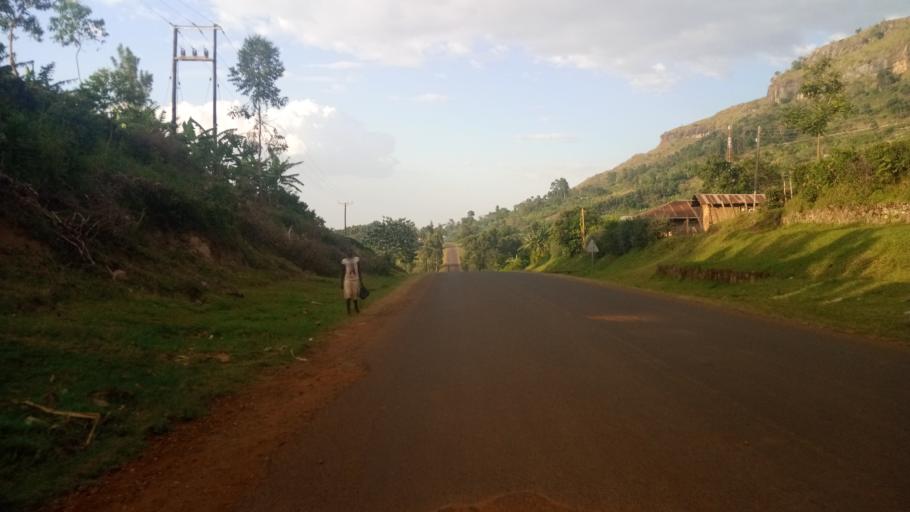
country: UG
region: Eastern Region
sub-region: Kapchorwa District
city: Kapchorwa
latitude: 1.3280
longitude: 34.3566
